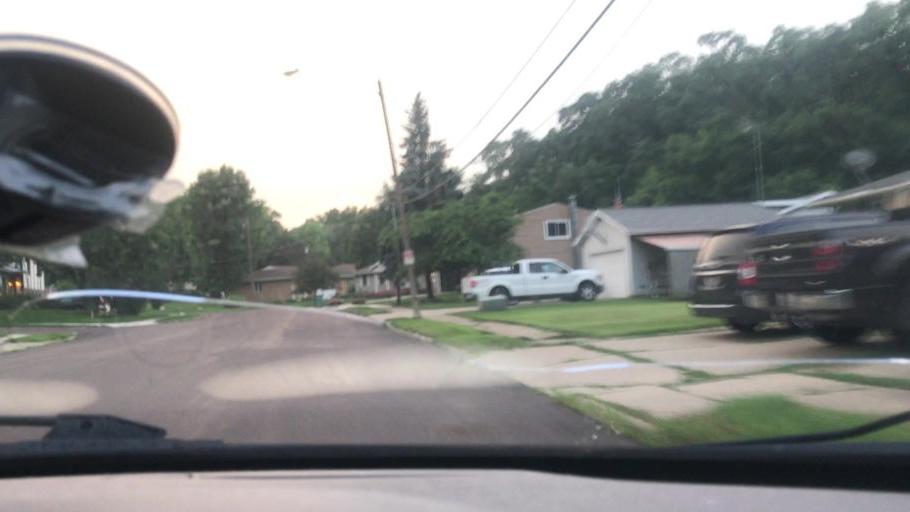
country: US
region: Illinois
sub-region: Tazewell County
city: Pekin
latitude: 40.5563
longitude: -89.6166
